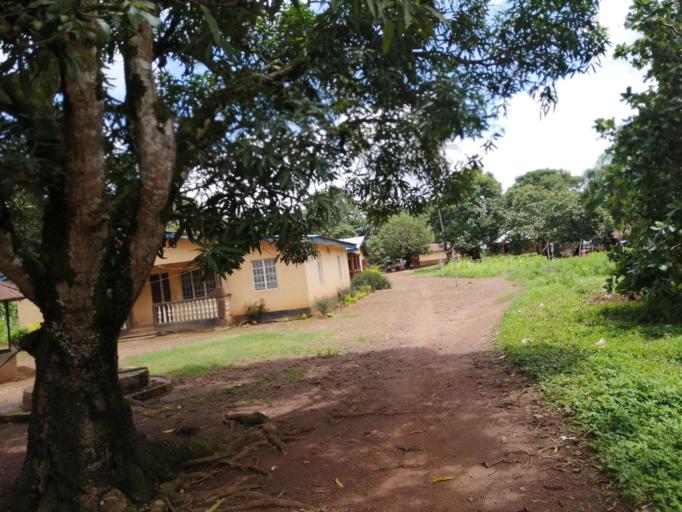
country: SL
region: Northern Province
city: Port Loko
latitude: 8.7767
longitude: -12.7971
